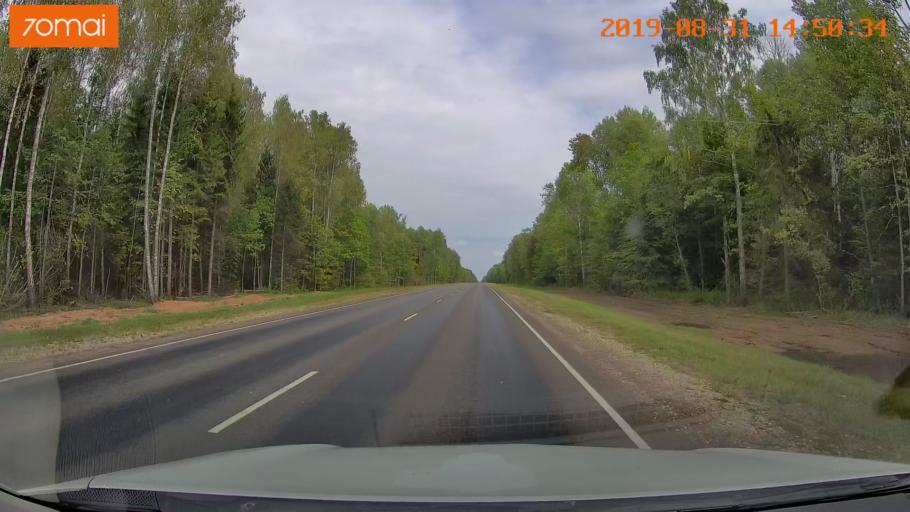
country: RU
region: Kaluga
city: Spas-Demensk
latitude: 54.2623
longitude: 33.7930
